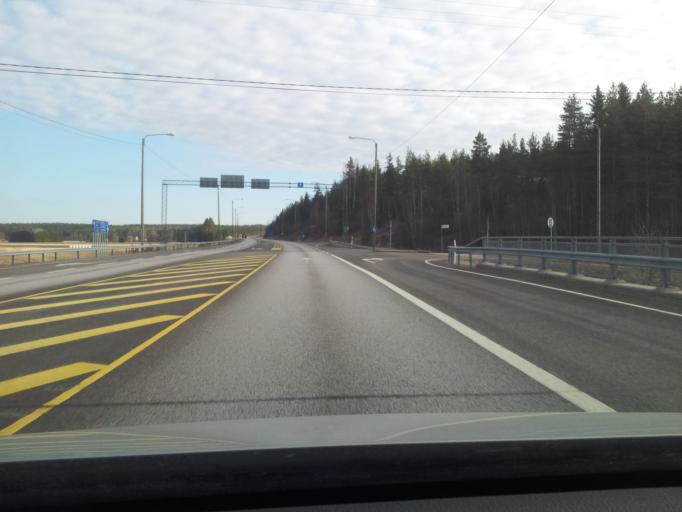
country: FI
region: Uusimaa
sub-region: Loviisa
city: Liljendal
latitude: 60.5717
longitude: 26.0709
